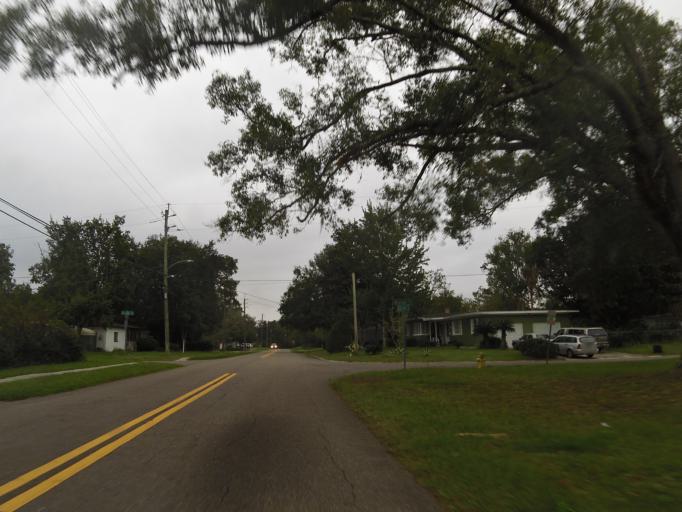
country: US
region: Florida
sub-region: Clay County
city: Bellair-Meadowbrook Terrace
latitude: 30.2761
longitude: -81.7437
